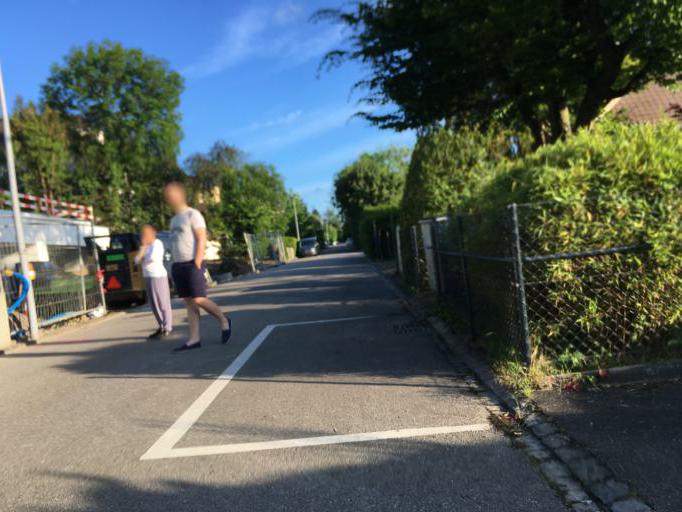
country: CH
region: Zurich
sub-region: Bezirk Meilen
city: Zollikon
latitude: 47.3456
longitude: 8.5787
